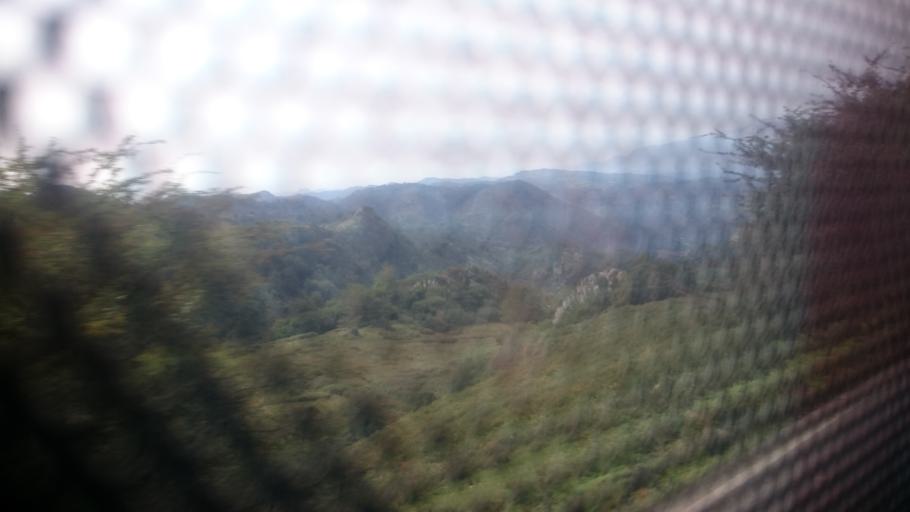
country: ES
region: Asturias
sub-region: Province of Asturias
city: Amieva
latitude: 43.2914
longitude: -5.0159
